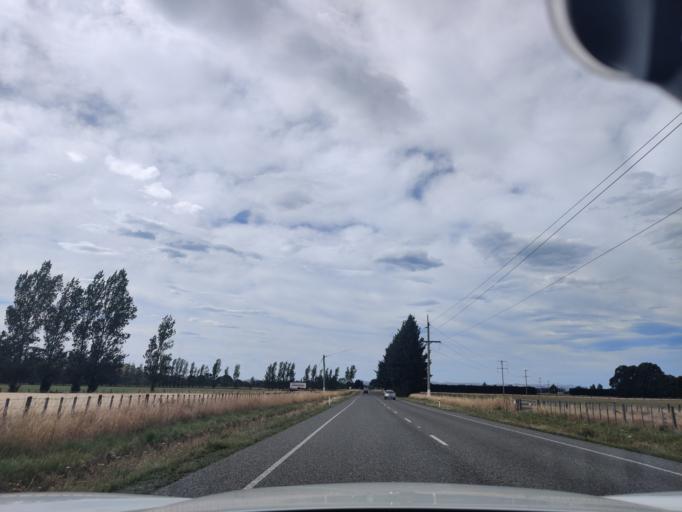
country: NZ
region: Wellington
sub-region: Masterton District
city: Masterton
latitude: -40.8519
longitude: 175.6368
